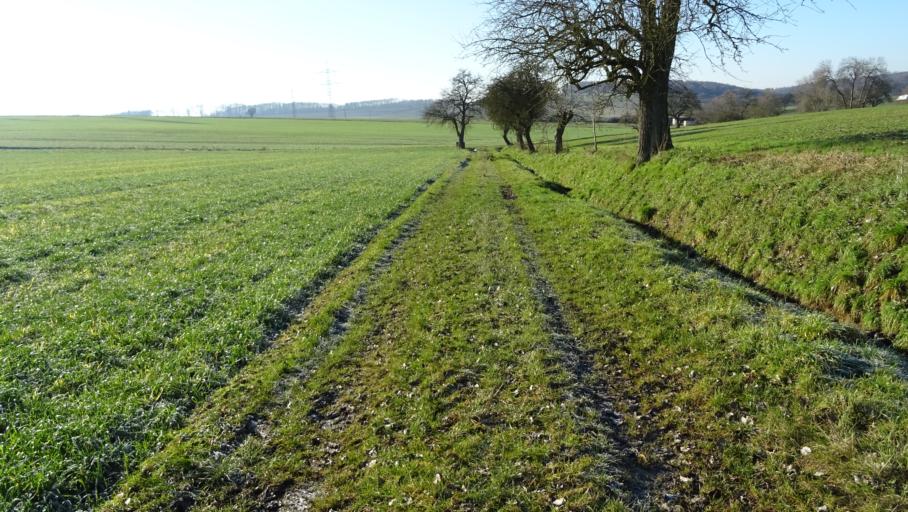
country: DE
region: Baden-Wuerttemberg
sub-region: Karlsruhe Region
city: Mosbach
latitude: 49.3423
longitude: 9.1841
